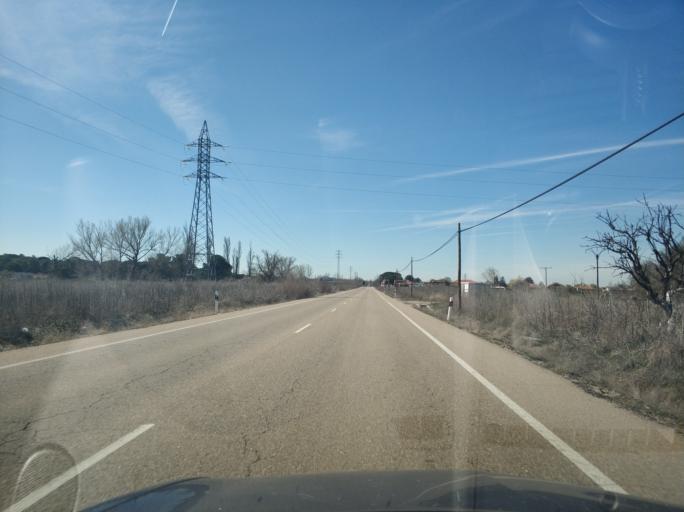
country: ES
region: Castille and Leon
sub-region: Provincia de Valladolid
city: Tudela de Duero
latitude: 41.5841
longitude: -4.5622
